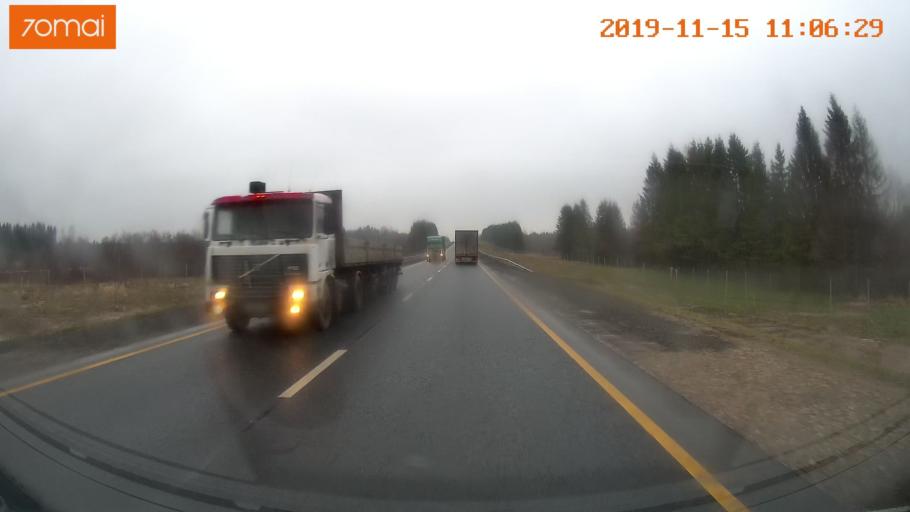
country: RU
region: Vologda
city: Chebsara
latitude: 59.1190
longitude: 39.0281
